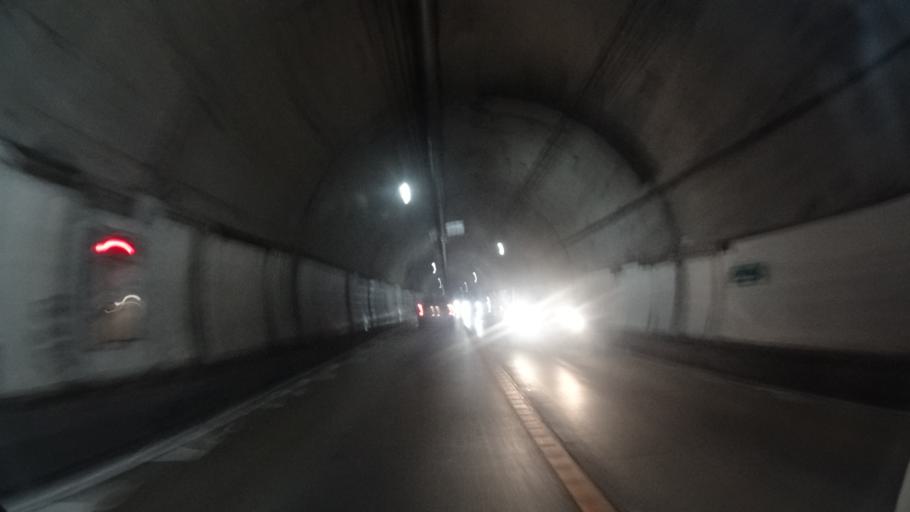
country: JP
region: Shimane
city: Masuda
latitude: 34.6694
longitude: 131.7122
